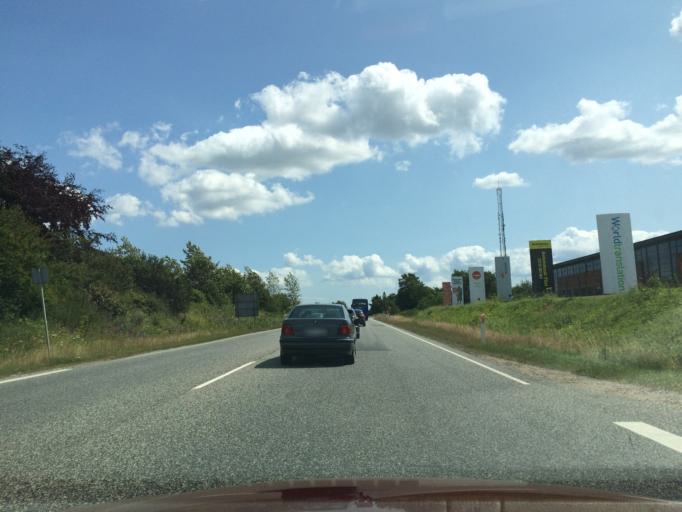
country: DK
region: Central Jutland
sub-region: Favrskov Kommune
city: Soften
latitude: 56.1862
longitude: 10.0920
